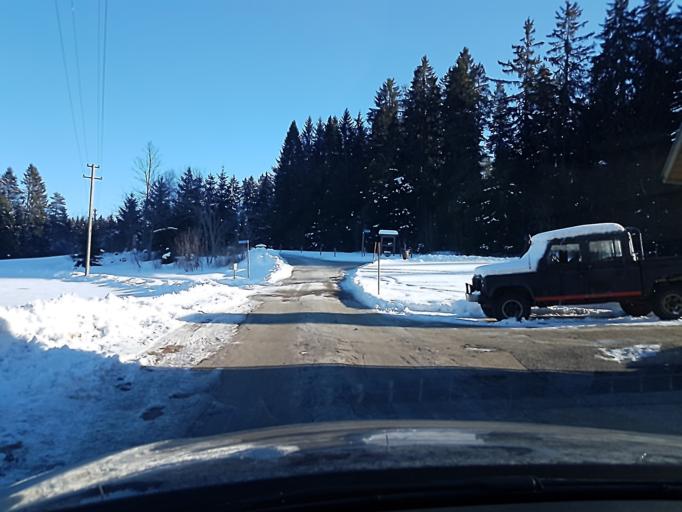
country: DE
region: Baden-Wuerttemberg
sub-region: Freiburg Region
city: Unterkirnach
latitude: 48.1029
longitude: 8.3574
